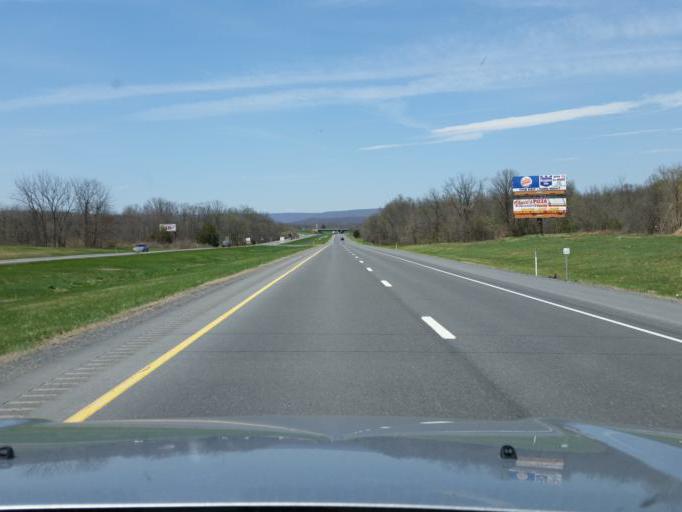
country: US
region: Pennsylvania
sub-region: Juniata County
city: Mifflintown
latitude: 40.5466
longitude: -77.3517
